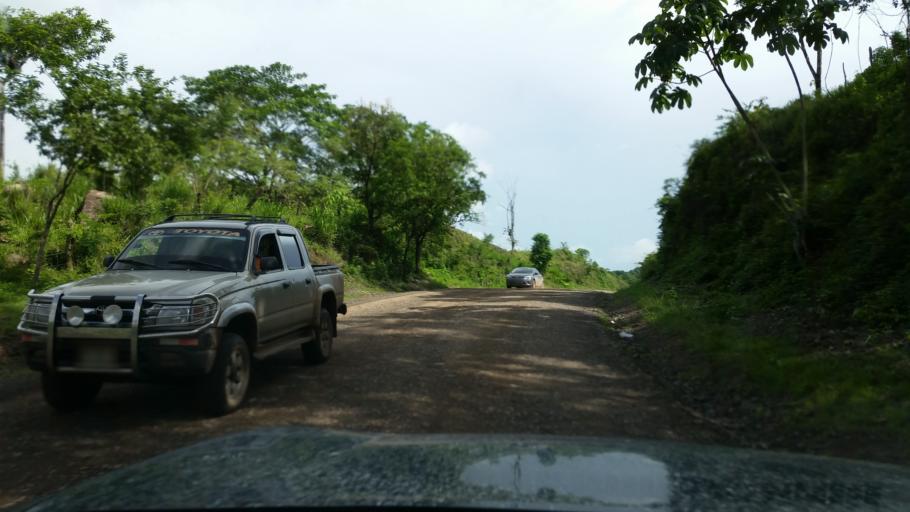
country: NI
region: Atlantico Norte (RAAN)
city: Siuna
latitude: 13.6542
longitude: -84.7934
